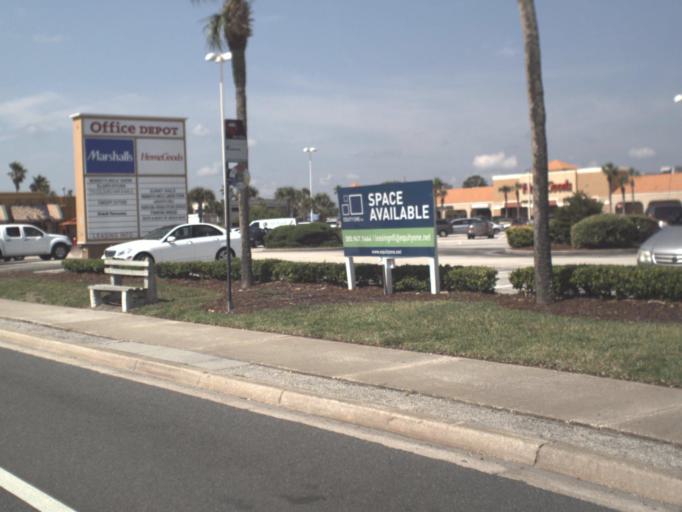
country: US
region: Florida
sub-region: Duval County
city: Jacksonville Beach
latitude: 30.2707
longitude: -81.3887
